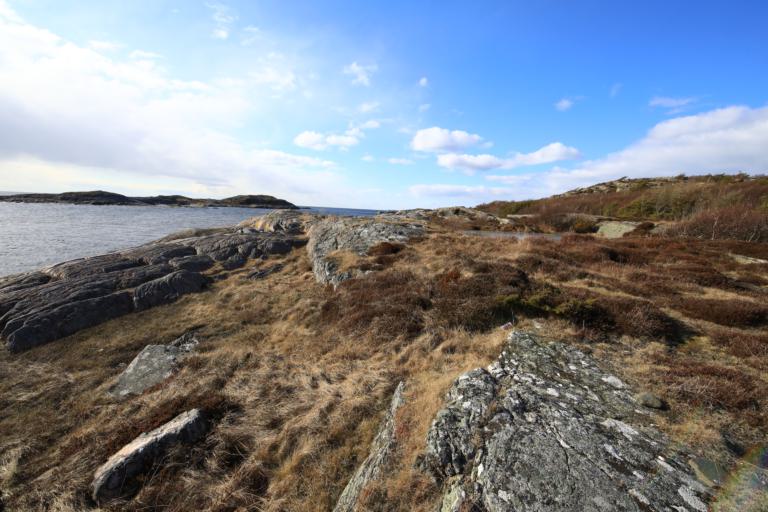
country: SE
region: Halland
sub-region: Kungsbacka Kommun
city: Frillesas
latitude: 57.2133
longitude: 12.1449
